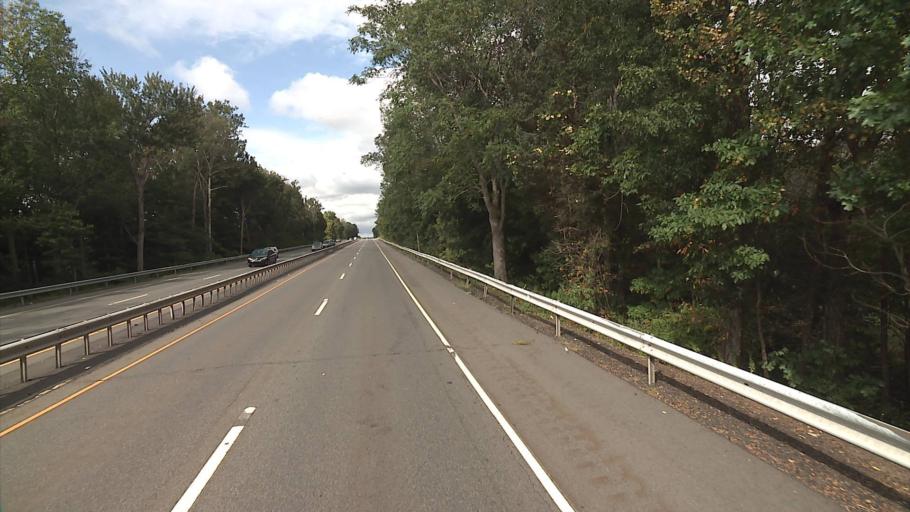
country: US
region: Connecticut
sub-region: New Haven County
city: Meriden
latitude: 41.5469
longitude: -72.7726
